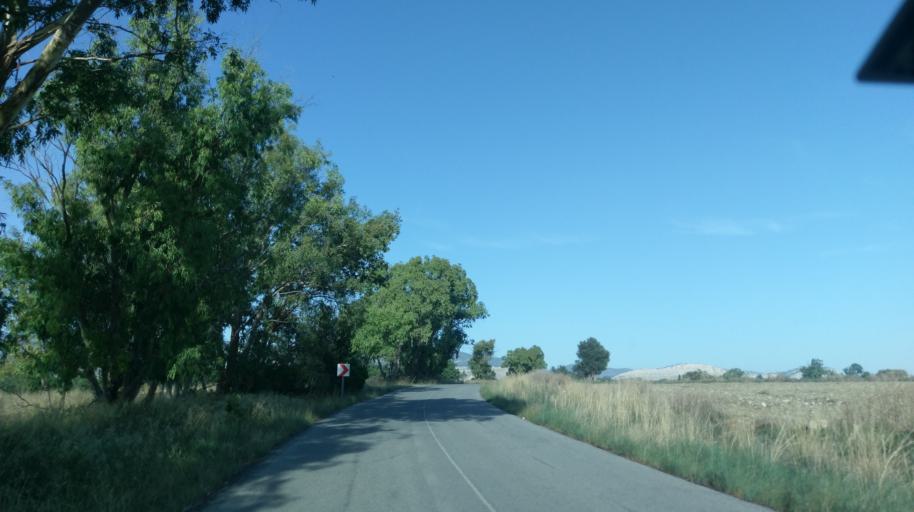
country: CY
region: Ammochostos
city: Lefkonoiko
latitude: 35.2949
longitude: 33.7385
